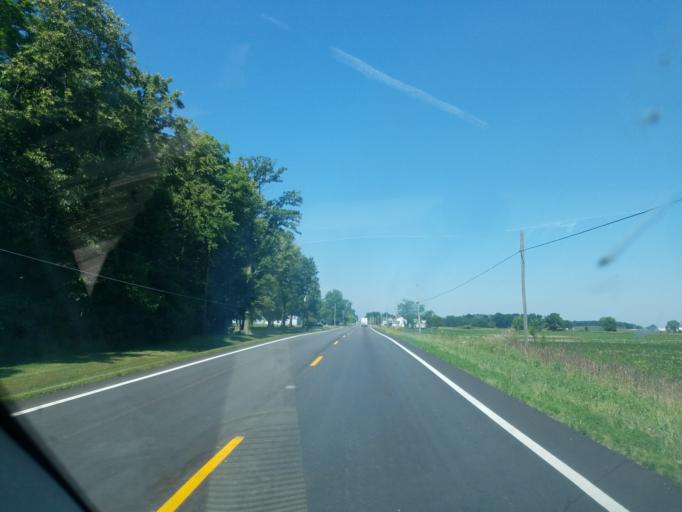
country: US
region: Ohio
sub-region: Shelby County
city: Jackson Center
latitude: 40.4395
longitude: -84.0837
